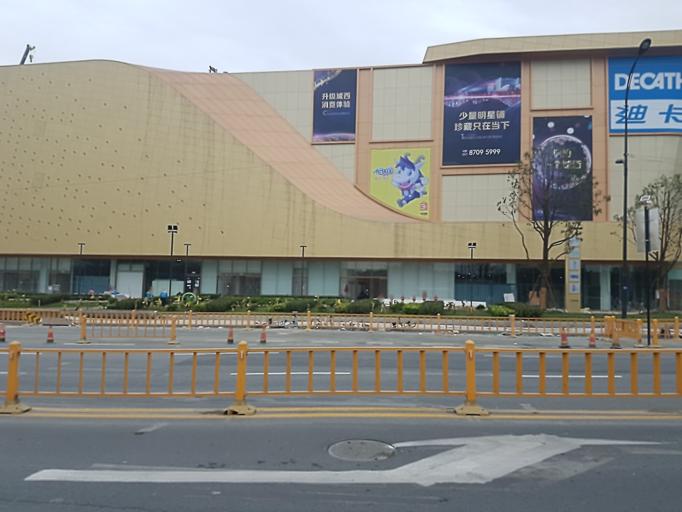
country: CN
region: Zhejiang Sheng
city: Jiangcun
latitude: 30.2967
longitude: 120.0698
